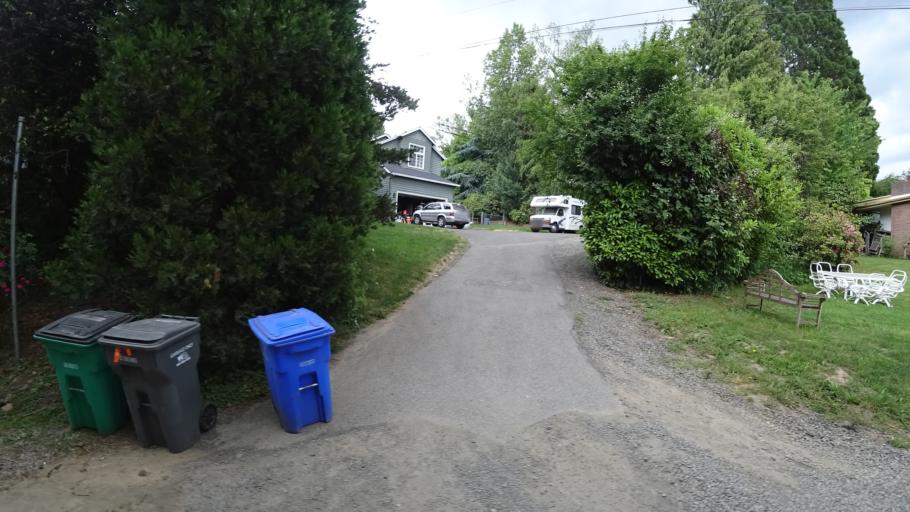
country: US
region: Oregon
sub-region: Clackamas County
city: Lake Oswego
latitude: 45.4597
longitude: -122.6983
